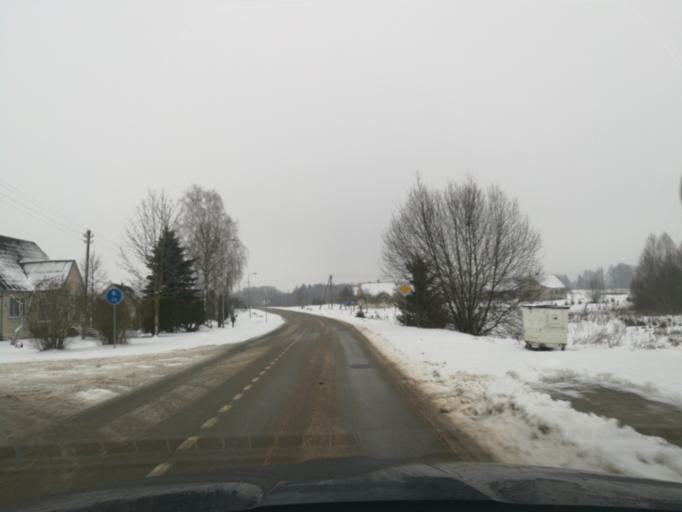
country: LT
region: Utenos apskritis
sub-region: Anyksciai
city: Anyksciai
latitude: 55.4178
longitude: 25.0610
